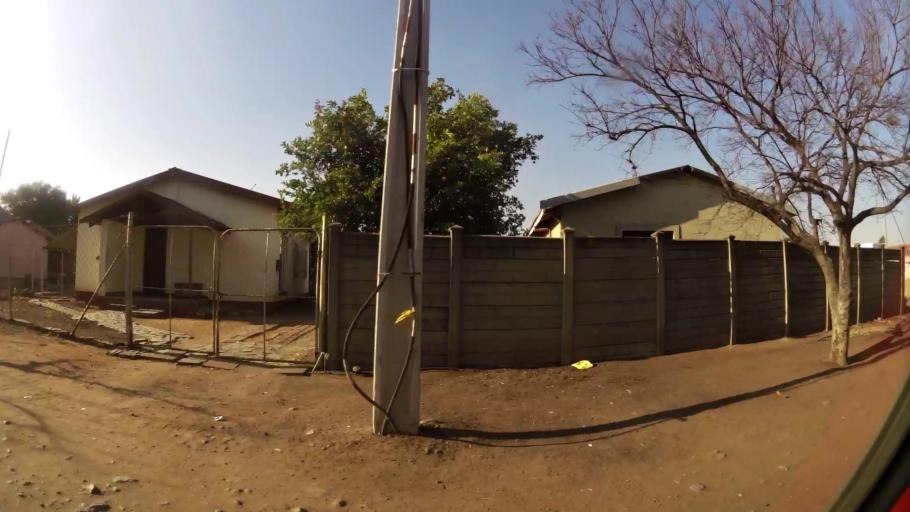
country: ZA
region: North-West
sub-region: Bojanala Platinum District Municipality
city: Rustenburg
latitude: -25.6441
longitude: 27.2388
